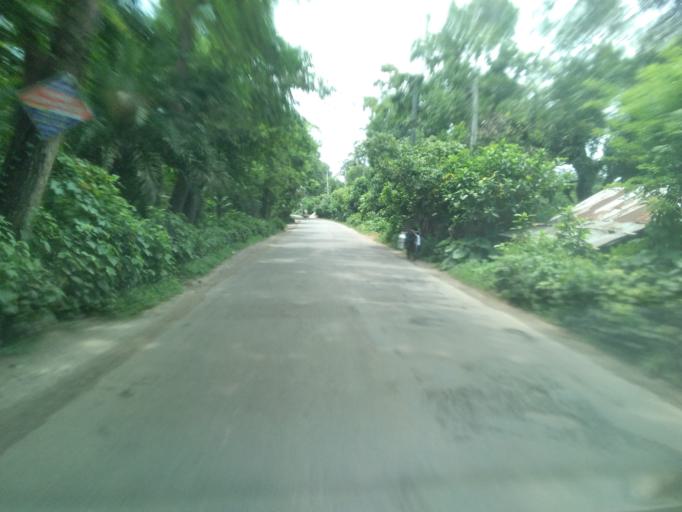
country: IN
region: West Bengal
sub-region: North 24 Parganas
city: Taki
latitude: 22.5599
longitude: 89.0048
